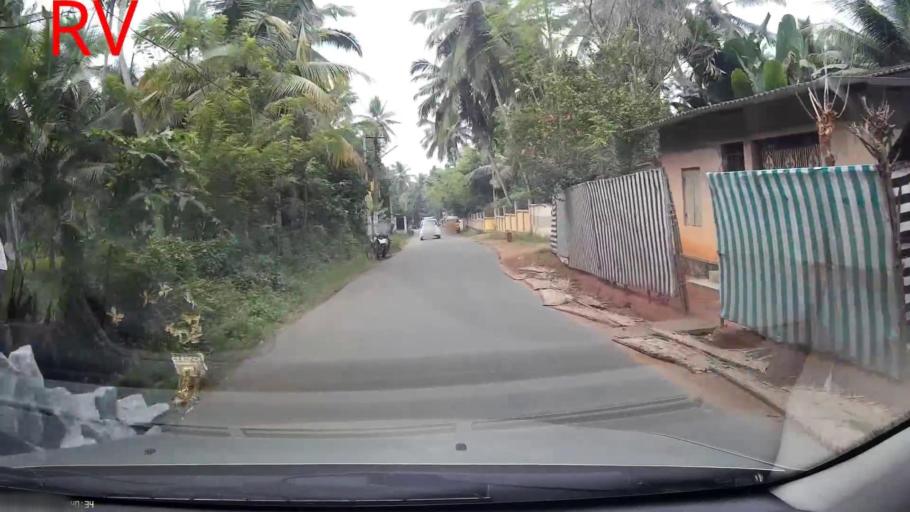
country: IN
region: Kerala
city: Kovalam
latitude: 8.3988
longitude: 77.0204
